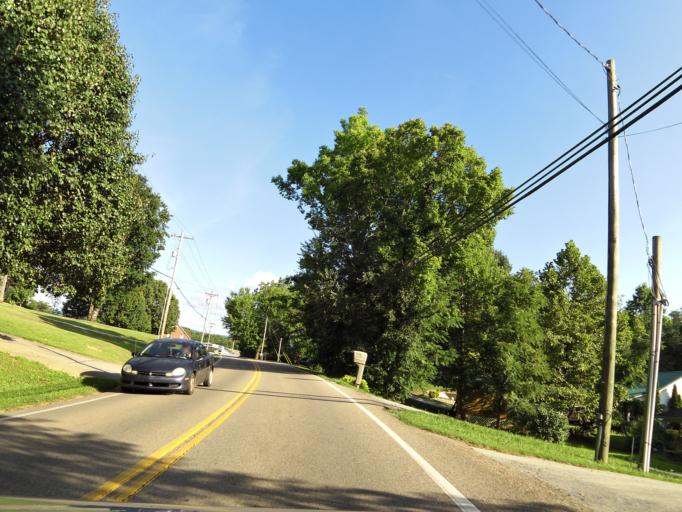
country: US
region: Tennessee
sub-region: Blount County
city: Maryville
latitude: 35.7041
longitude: -83.9668
